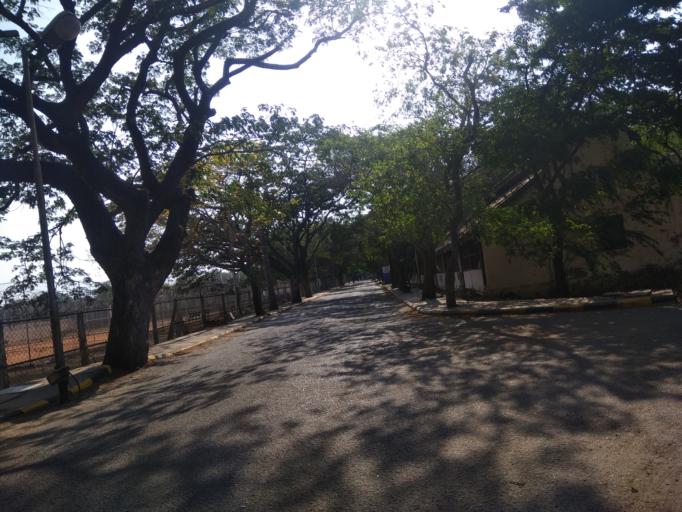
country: IN
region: Tamil Nadu
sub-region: Chennai
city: Gandhi Nagar
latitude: 13.0123
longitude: 80.2394
